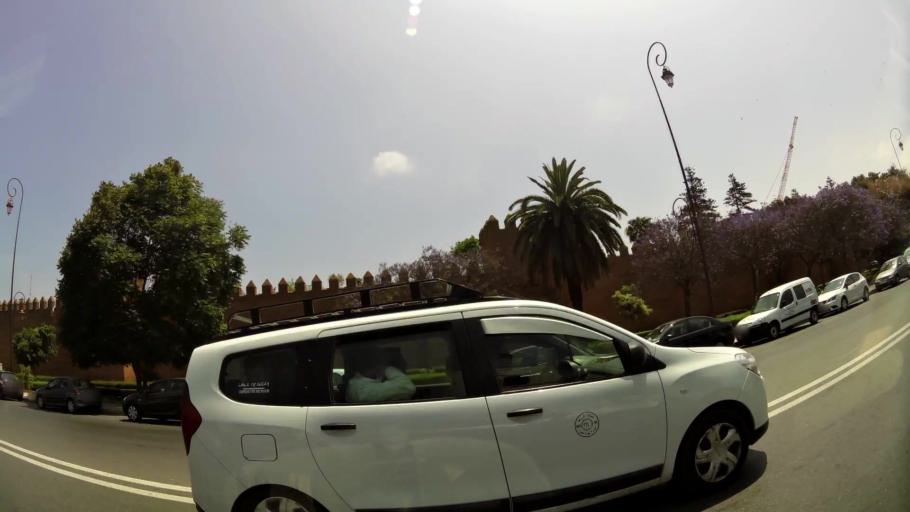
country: MA
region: Rabat-Sale-Zemmour-Zaer
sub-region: Rabat
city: Rabat
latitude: 34.0173
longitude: -6.8393
